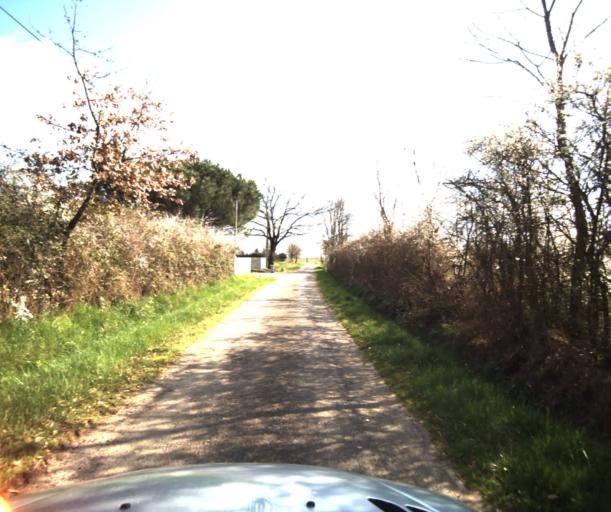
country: FR
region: Midi-Pyrenees
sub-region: Departement du Tarn-et-Garonne
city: Montbeton
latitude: 43.9722
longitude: 1.2928
